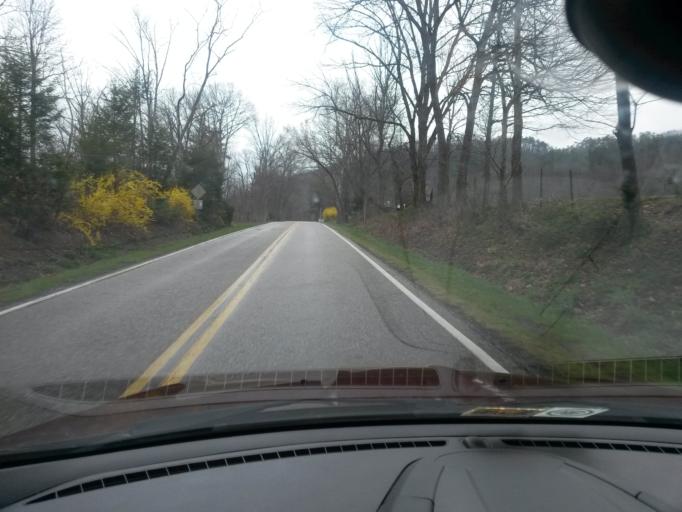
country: US
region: Virginia
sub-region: Alleghany County
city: Clifton Forge
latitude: 37.9119
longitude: -79.7272
